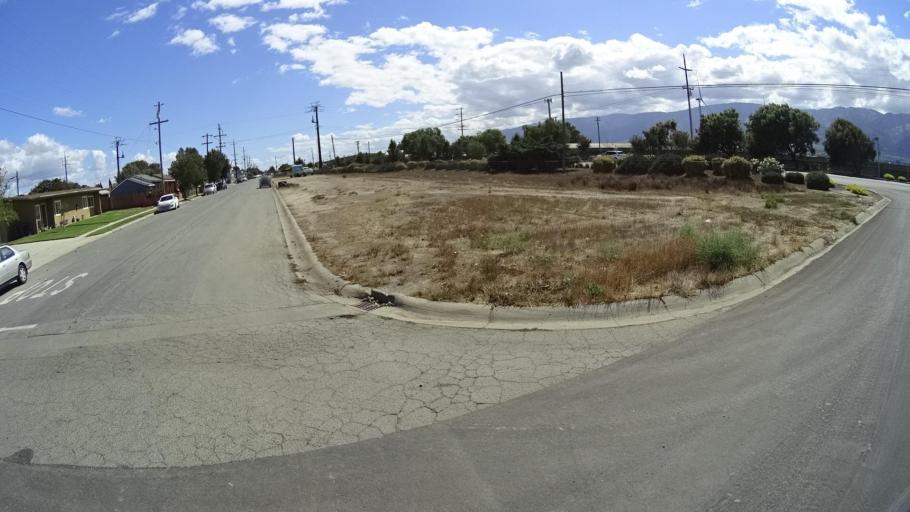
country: US
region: California
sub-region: Monterey County
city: Gonzales
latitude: 36.5114
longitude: -121.4503
